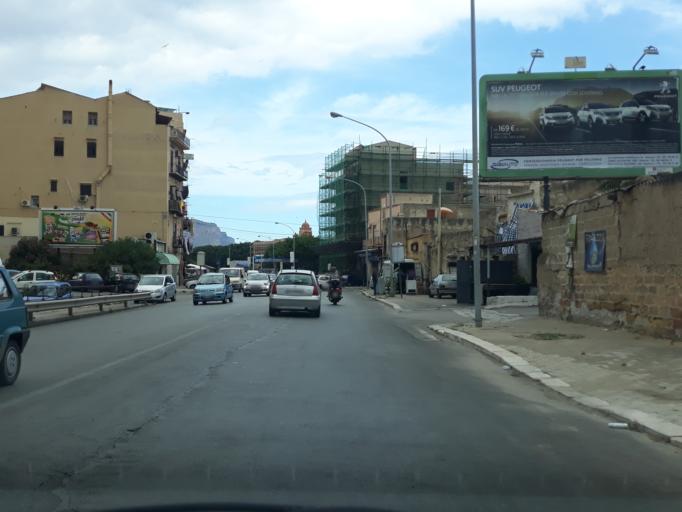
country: IT
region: Sicily
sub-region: Palermo
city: Ciaculli
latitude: 38.1111
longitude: 13.3785
